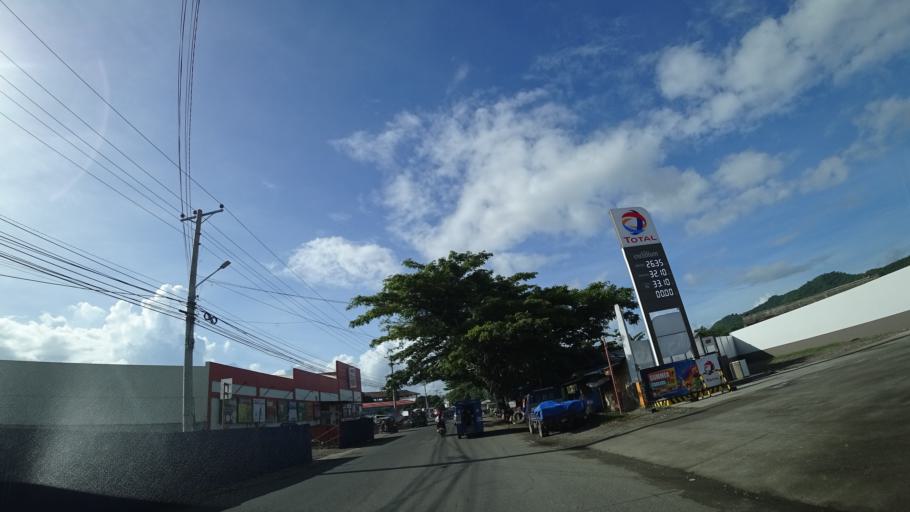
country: PH
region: Eastern Visayas
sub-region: Province of Leyte
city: Panalanoy
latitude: 11.2195
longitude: 124.9933
